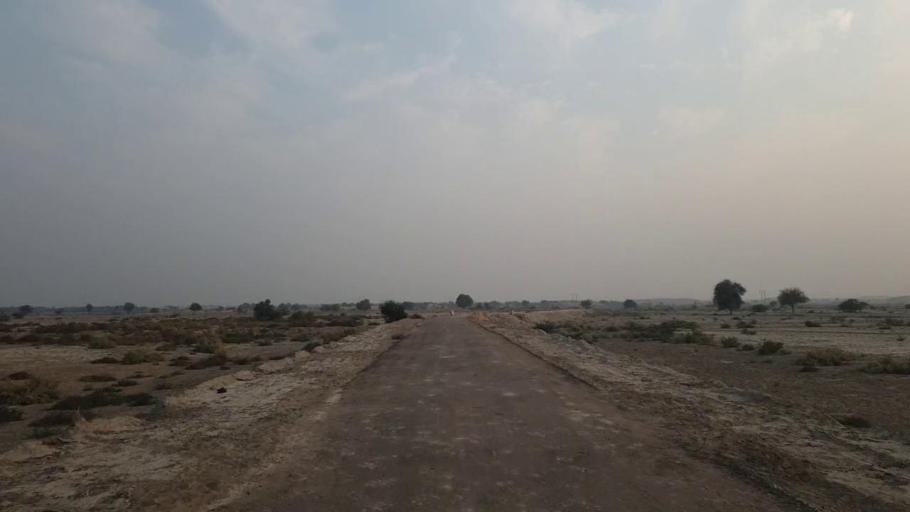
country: PK
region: Sindh
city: Sann
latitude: 26.1771
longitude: 67.9907
